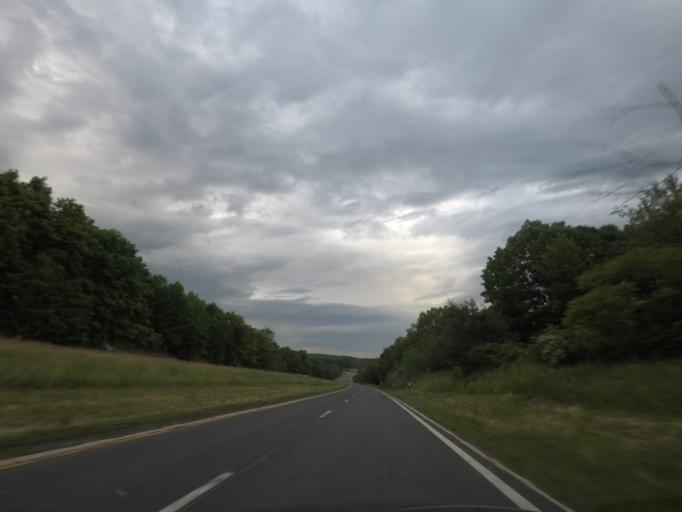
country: US
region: New York
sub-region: Columbia County
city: Philmont
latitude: 42.2005
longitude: -73.6367
